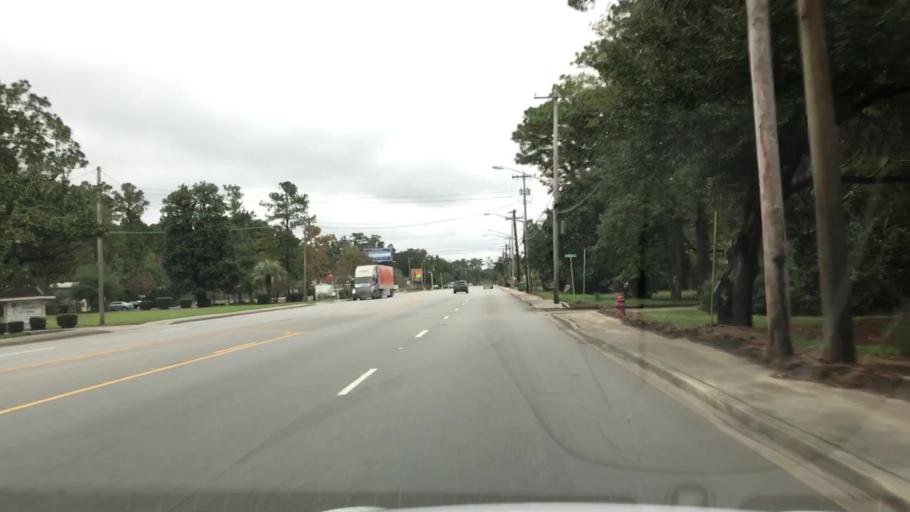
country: US
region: South Carolina
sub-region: Georgetown County
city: Georgetown
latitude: 33.3461
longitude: -79.2968
